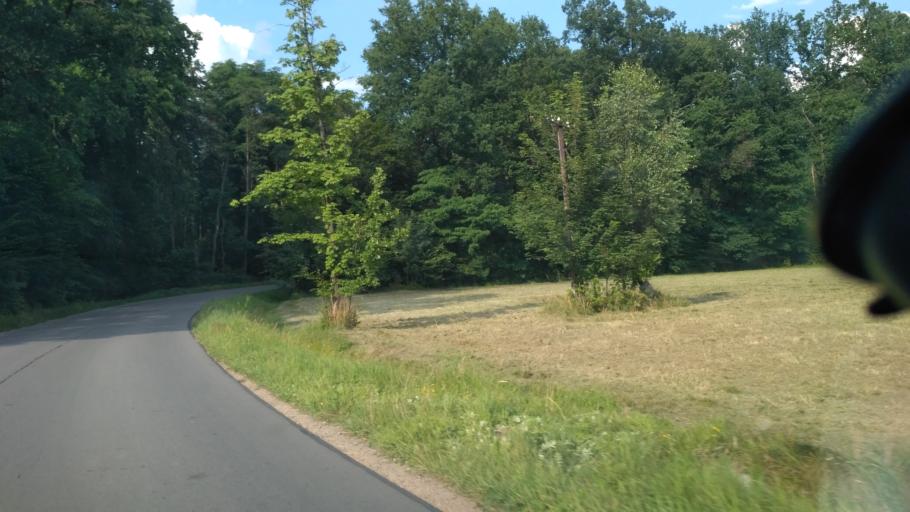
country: PL
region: Subcarpathian Voivodeship
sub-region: Powiat rzeszowski
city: Glogow Malopolski
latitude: 50.1595
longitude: 21.9828
